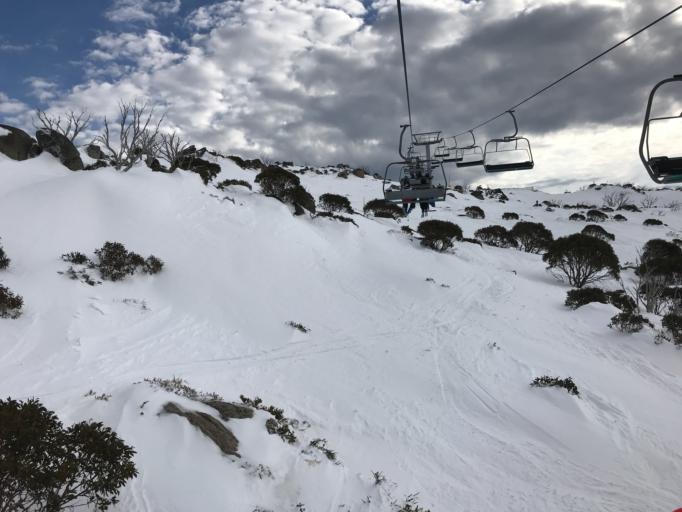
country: AU
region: New South Wales
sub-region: Snowy River
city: Jindabyne
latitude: -36.3776
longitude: 148.3984
